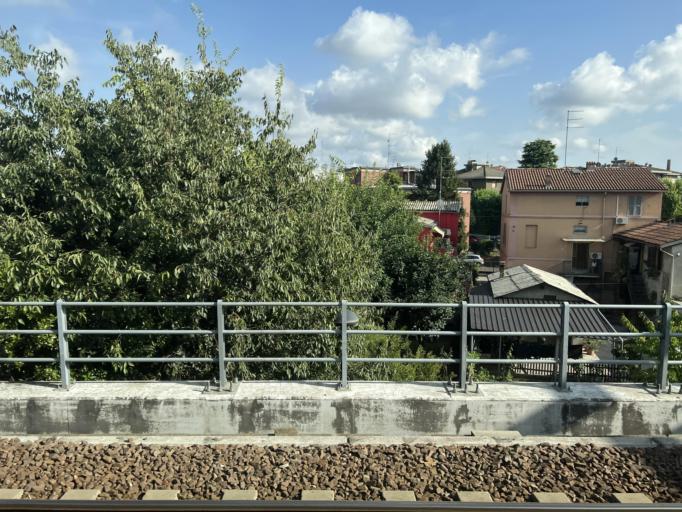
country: IT
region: Emilia-Romagna
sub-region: Provincia di Parma
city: Parma
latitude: 44.8078
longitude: 10.3436
